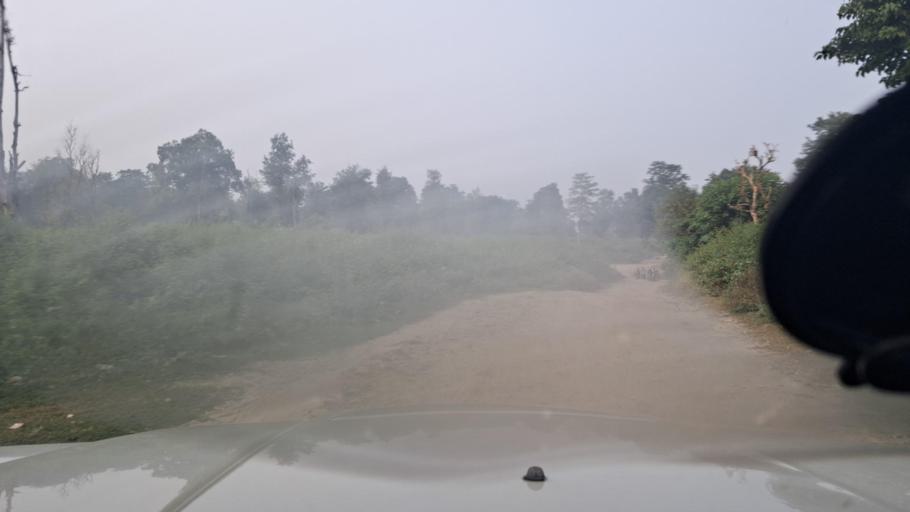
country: IN
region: Uttarakhand
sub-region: Udham Singh Nagar
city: Tanakpur
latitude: 29.0521
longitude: 80.1340
